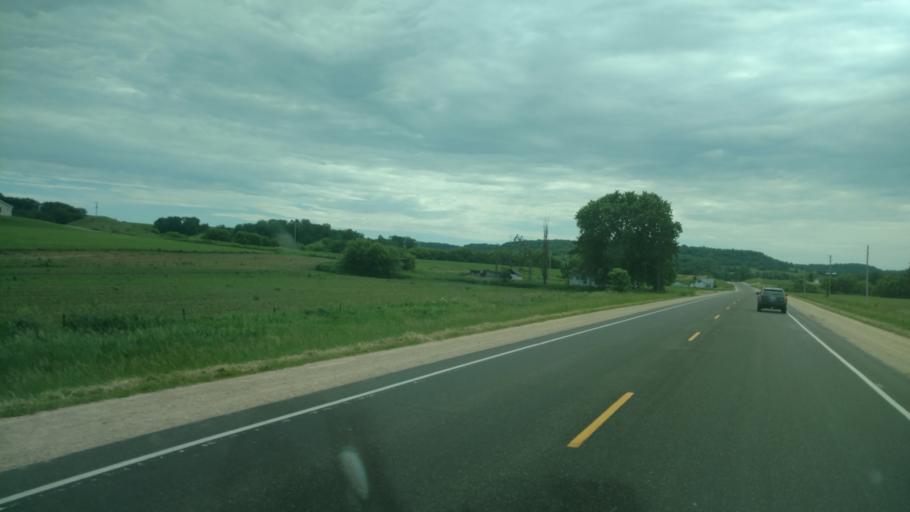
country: US
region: Wisconsin
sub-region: Monroe County
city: Tomah
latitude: 43.8440
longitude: -90.4739
